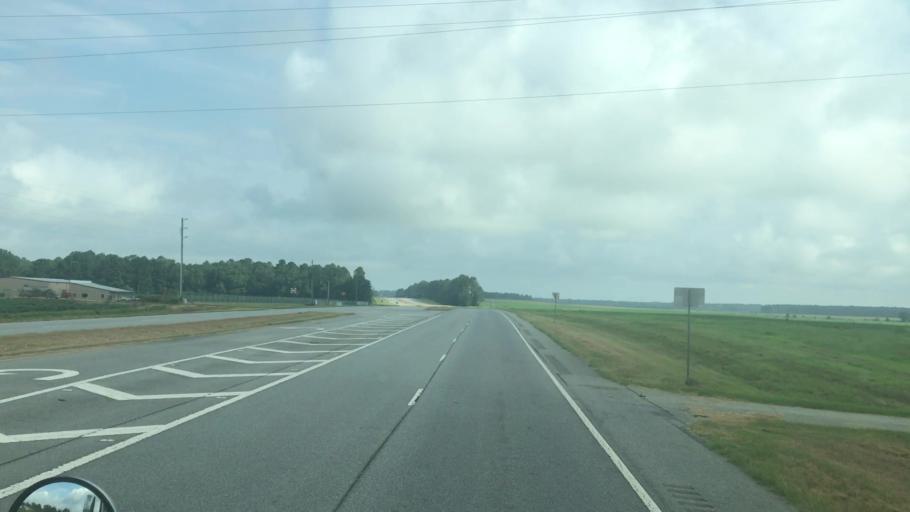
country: US
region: Georgia
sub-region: Miller County
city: Colquitt
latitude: 31.1840
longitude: -84.7623
